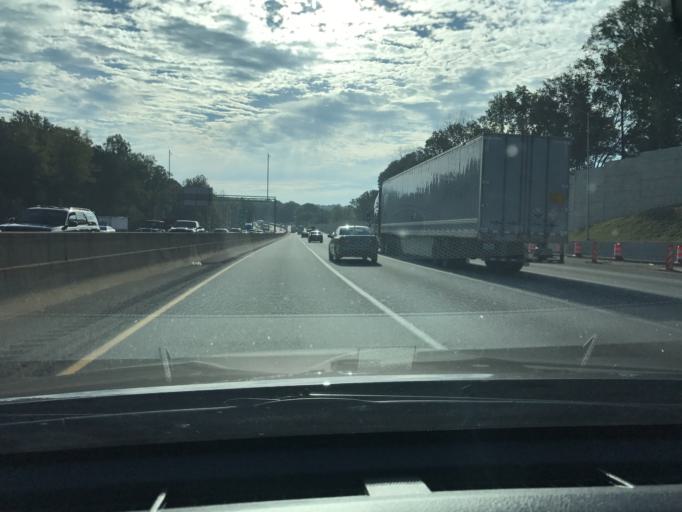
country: US
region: Georgia
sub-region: DeKalb County
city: Panthersville
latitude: 33.6987
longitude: -84.2639
